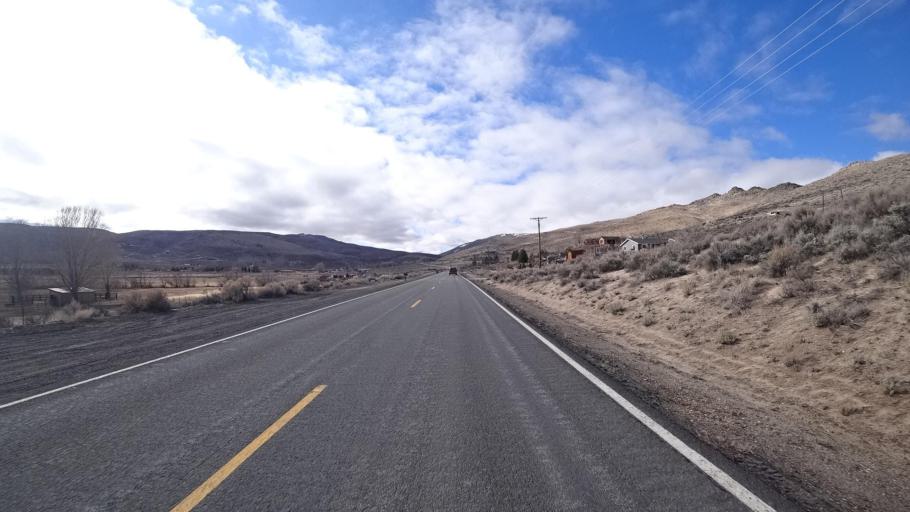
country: US
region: Nevada
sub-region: Washoe County
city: Cold Springs
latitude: 39.8511
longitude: -119.9351
